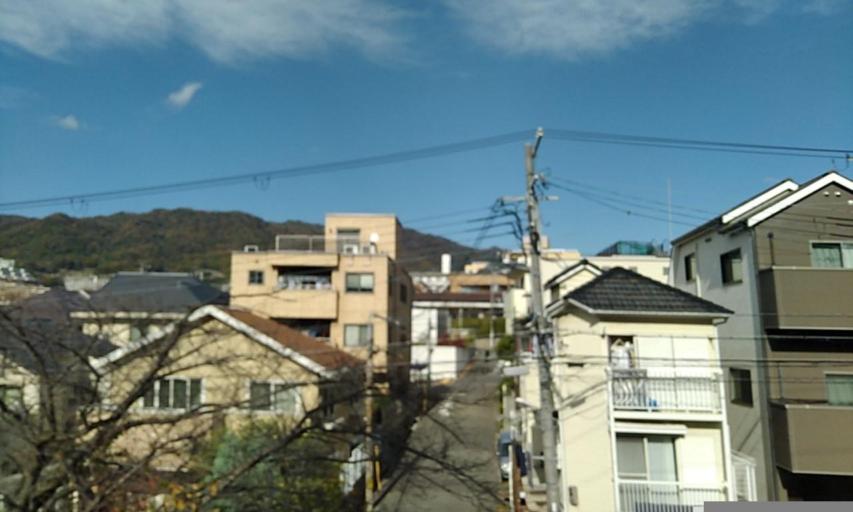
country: JP
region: Hyogo
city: Ashiya
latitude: 34.7408
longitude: 135.3135
